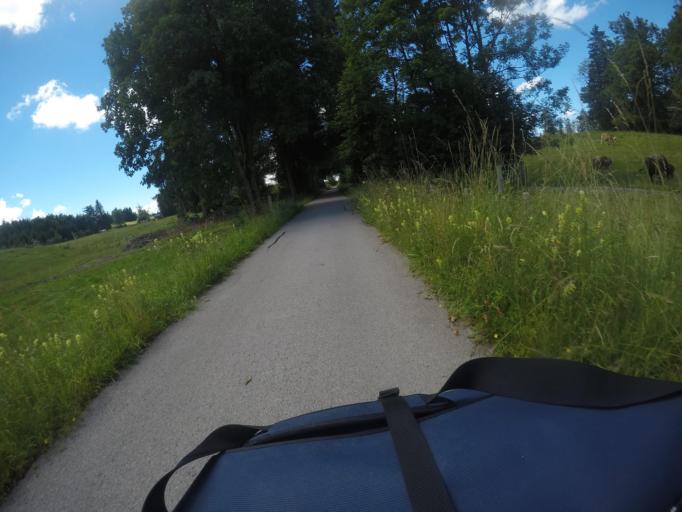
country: DE
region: Bavaria
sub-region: Swabia
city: Lechbruck
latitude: 47.6869
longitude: 10.7647
